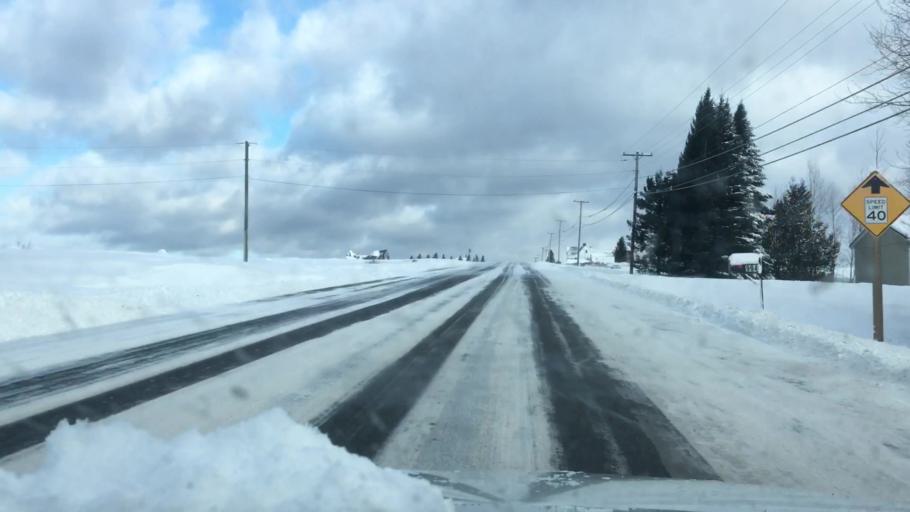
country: US
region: Maine
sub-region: Aroostook County
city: Caribou
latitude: 46.9347
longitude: -68.0233
